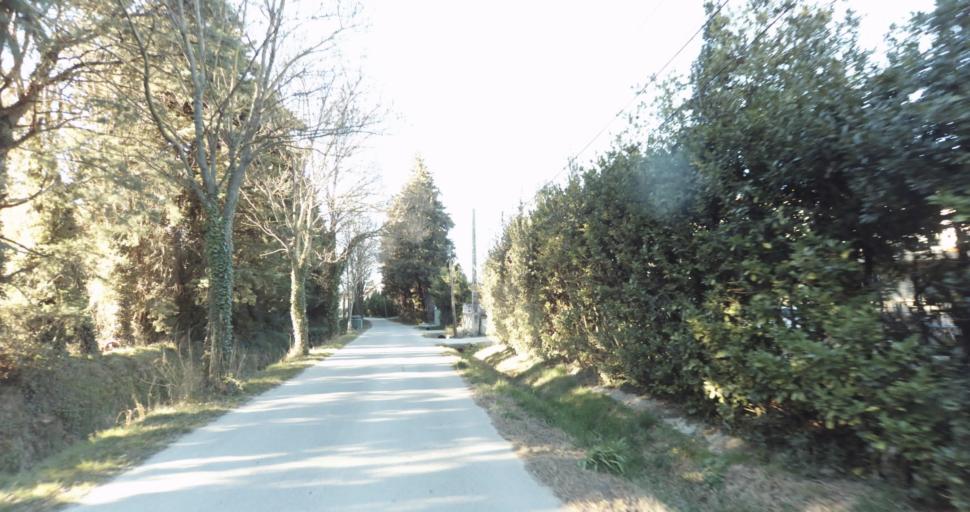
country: FR
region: Provence-Alpes-Cote d'Azur
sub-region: Departement des Bouches-du-Rhone
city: Barbentane
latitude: 43.9066
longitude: 4.7491
